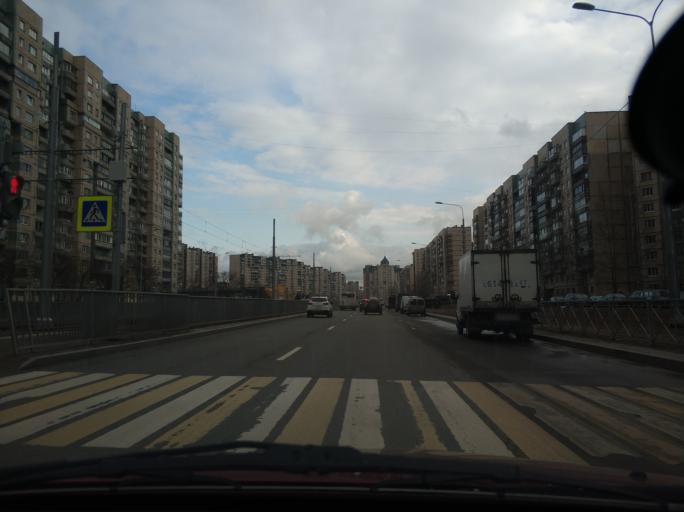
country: RU
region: St.-Petersburg
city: Krasnogvargeisky
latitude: 59.9524
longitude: 30.4842
